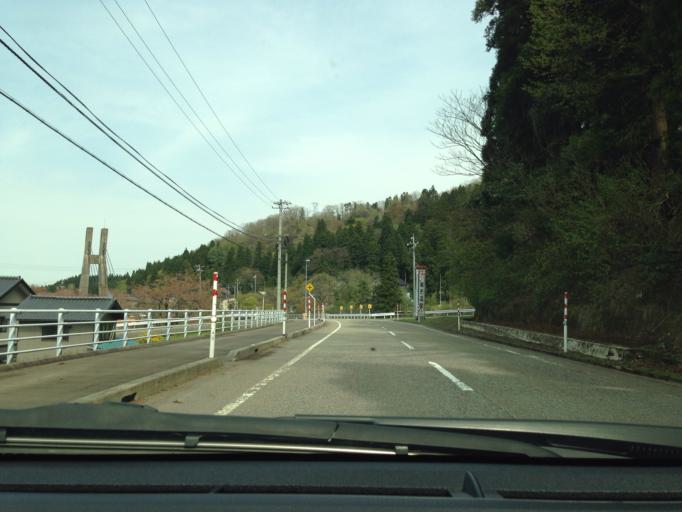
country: JP
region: Toyama
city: Fukumitsu
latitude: 36.4934
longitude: 136.8334
